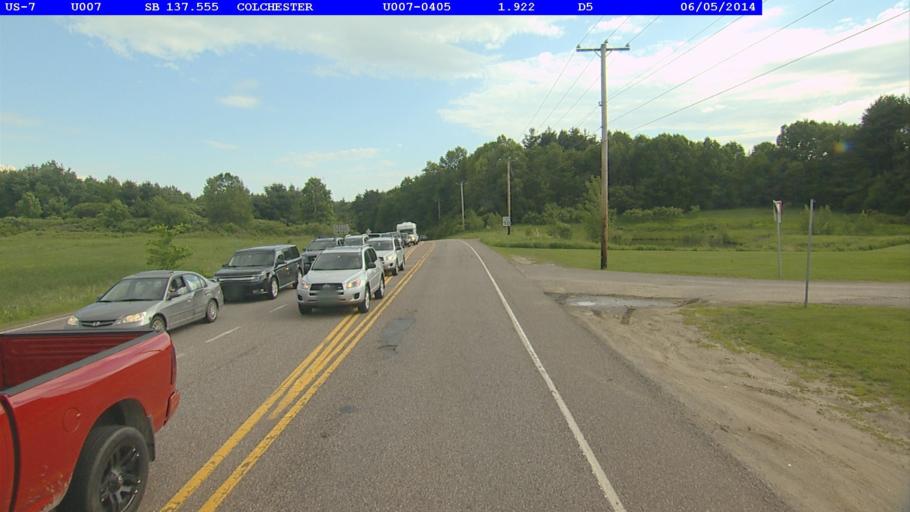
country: US
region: Vermont
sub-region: Chittenden County
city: Colchester
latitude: 44.5279
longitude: -73.1725
